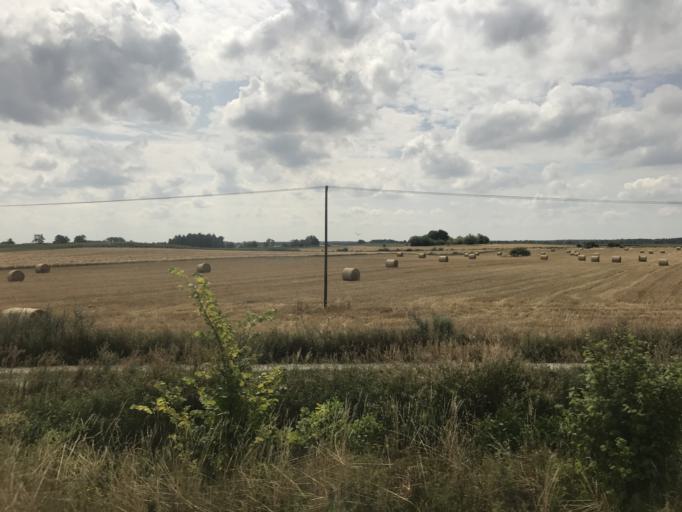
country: PL
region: Greater Poland Voivodeship
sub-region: Powiat poznanski
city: Pobiedziska
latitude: 52.4852
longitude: 17.3167
